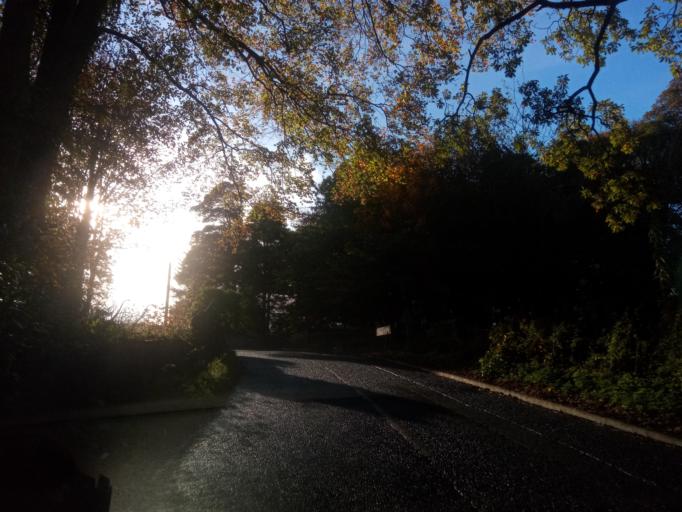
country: GB
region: Scotland
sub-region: The Scottish Borders
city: Eyemouth
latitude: 55.8474
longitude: -2.1165
